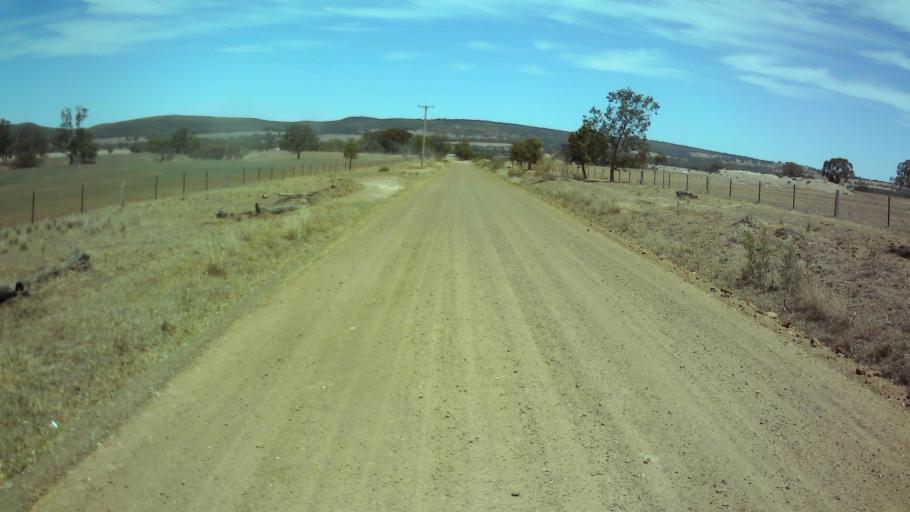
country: AU
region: New South Wales
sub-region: Weddin
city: Grenfell
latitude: -33.8238
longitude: 148.1695
